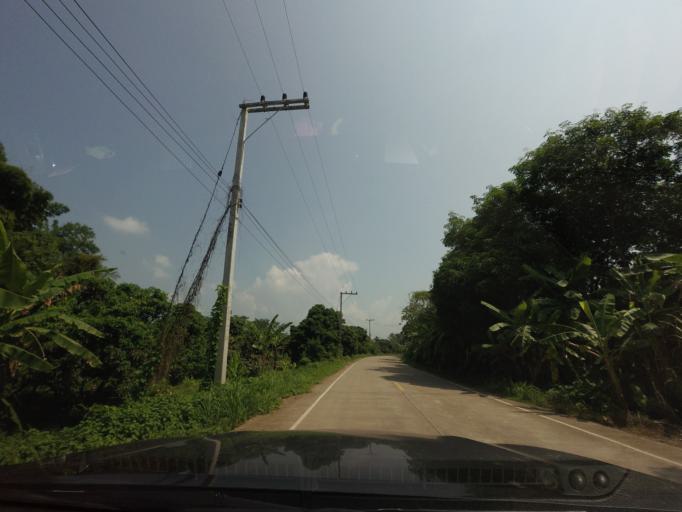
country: TH
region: Nan
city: Nan
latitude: 18.8592
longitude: 100.8080
